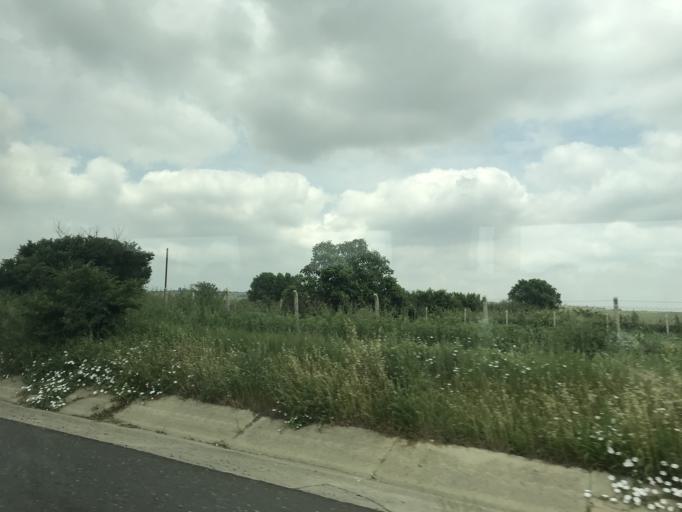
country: TR
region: Tekirdag
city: Tekirdag
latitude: 41.0059
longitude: 27.5371
